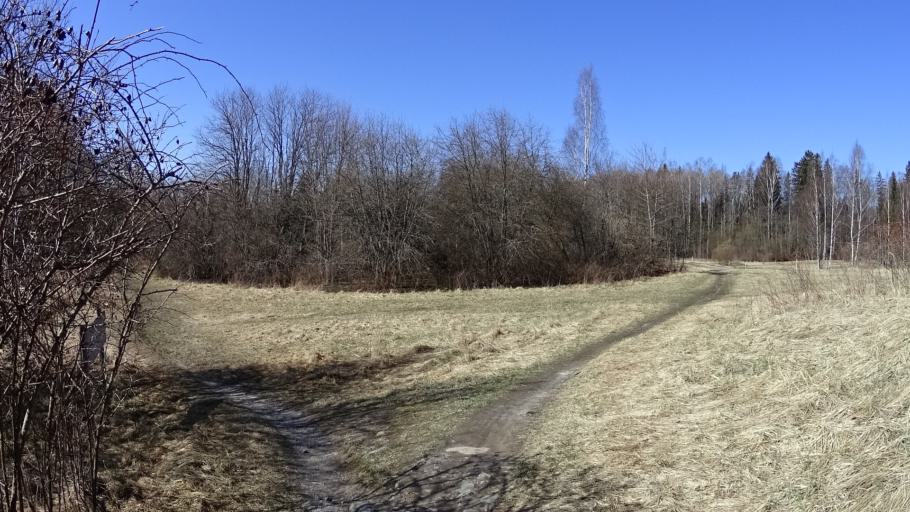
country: FI
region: Uusimaa
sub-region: Helsinki
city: Otaniemi
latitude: 60.2006
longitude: 24.8167
